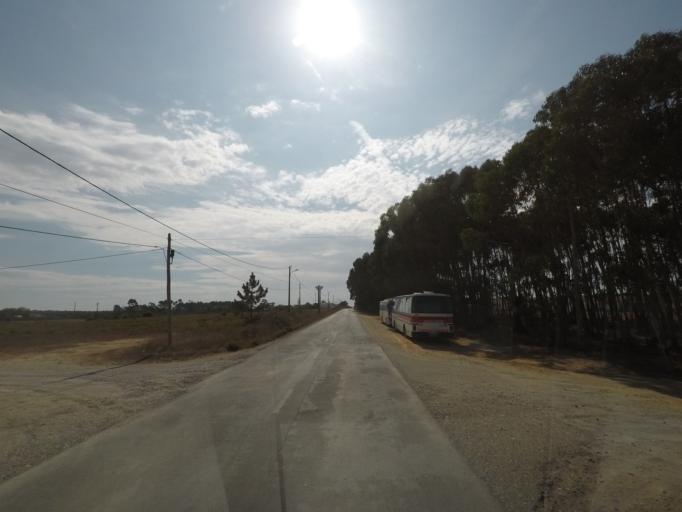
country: PT
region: Beja
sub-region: Odemira
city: Sao Teotonio
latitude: 37.4773
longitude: -8.7626
